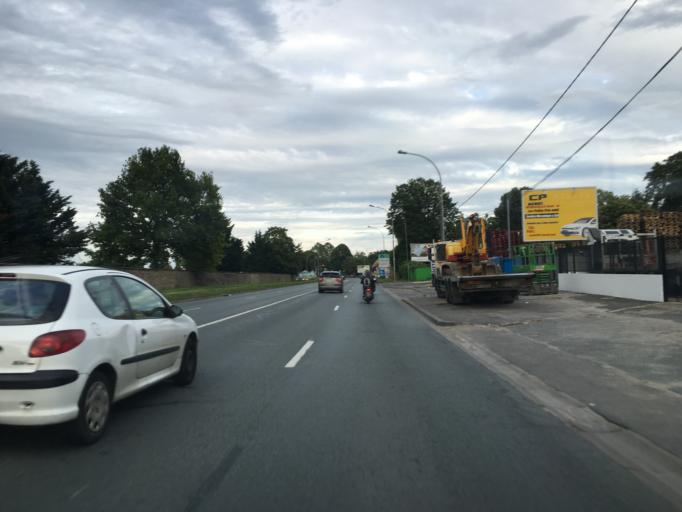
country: FR
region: Ile-de-France
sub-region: Departement du Val-de-Marne
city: Villecresnes
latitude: 48.7291
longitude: 2.5276
